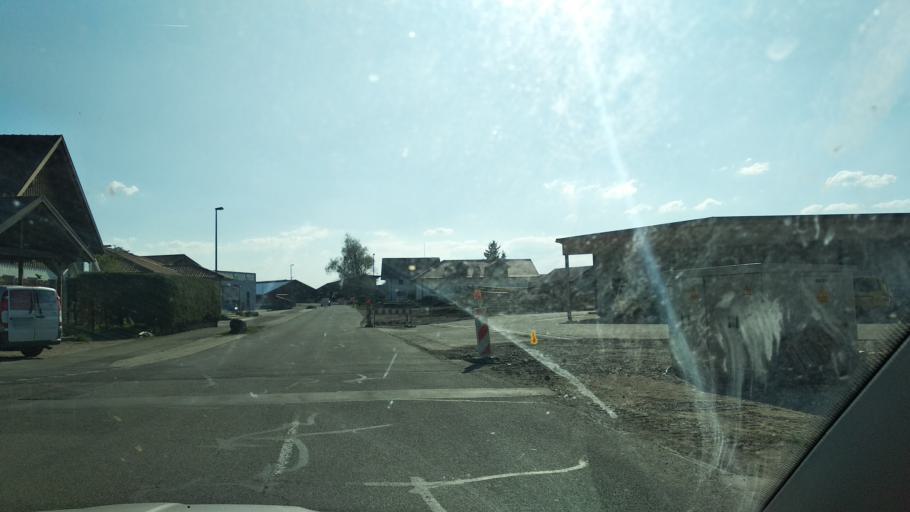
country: DE
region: Bavaria
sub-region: Swabia
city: Hawangen
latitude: 47.9677
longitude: 10.2565
